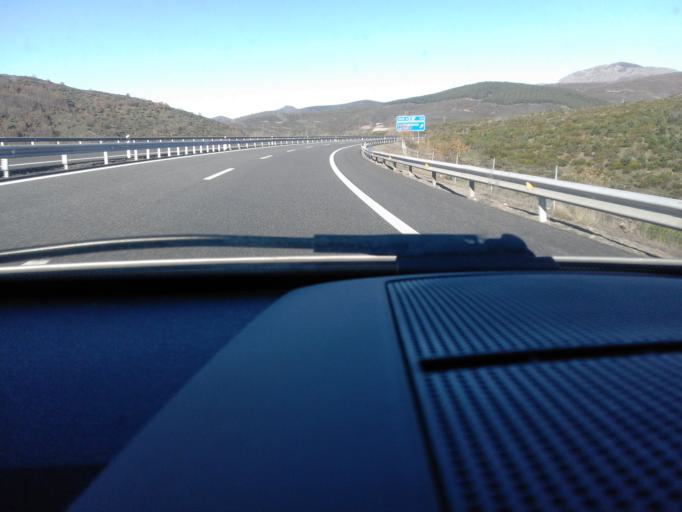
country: ES
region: Castille and Leon
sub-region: Provincia de Leon
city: Carrocera
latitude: 42.7692
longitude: -5.7806
